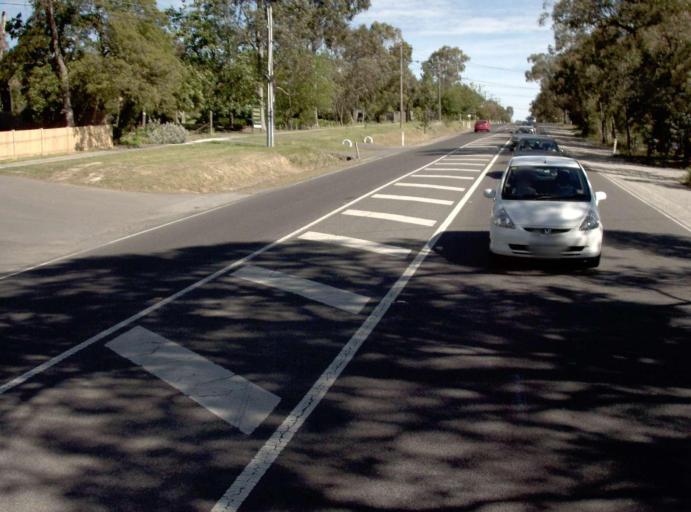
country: AU
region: Victoria
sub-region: Maroondah
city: Croydon South
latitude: -37.8193
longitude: 145.2691
